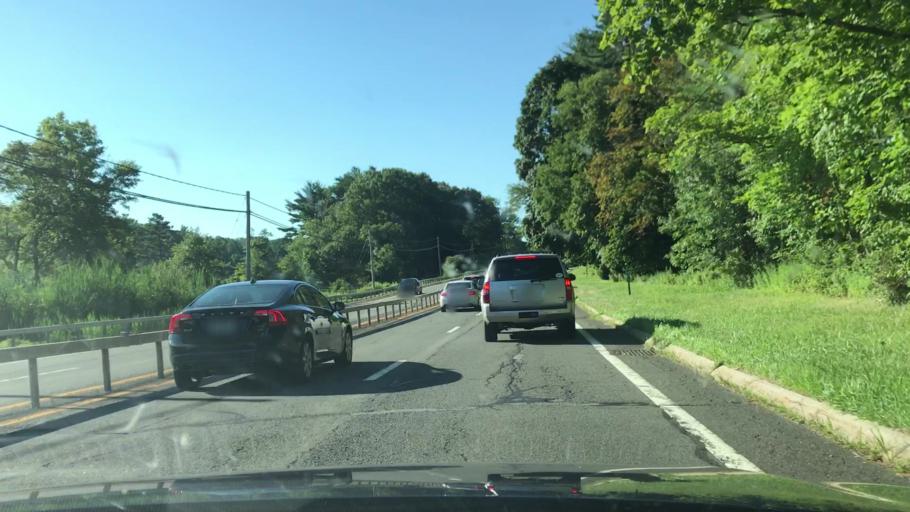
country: US
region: New York
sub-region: Westchester County
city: Hawthorne
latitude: 41.0912
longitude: -73.7919
